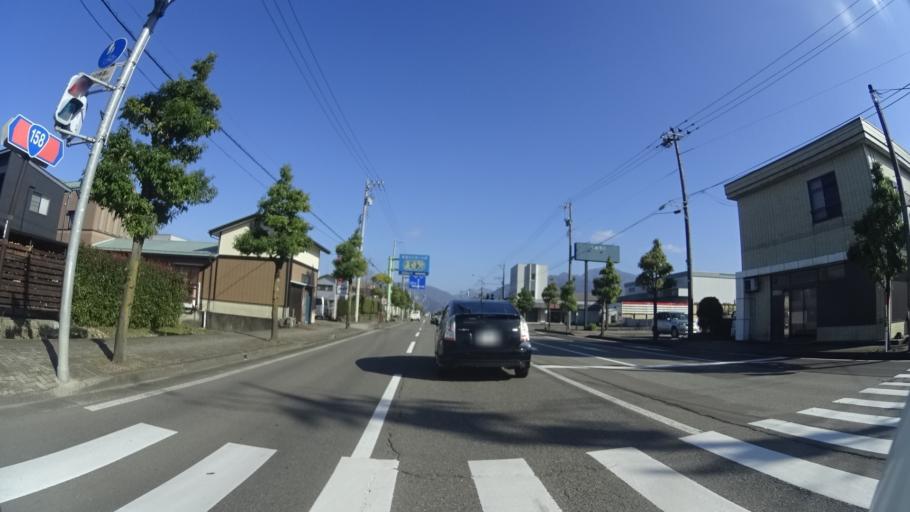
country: JP
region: Fukui
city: Ono
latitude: 35.9699
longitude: 136.4919
